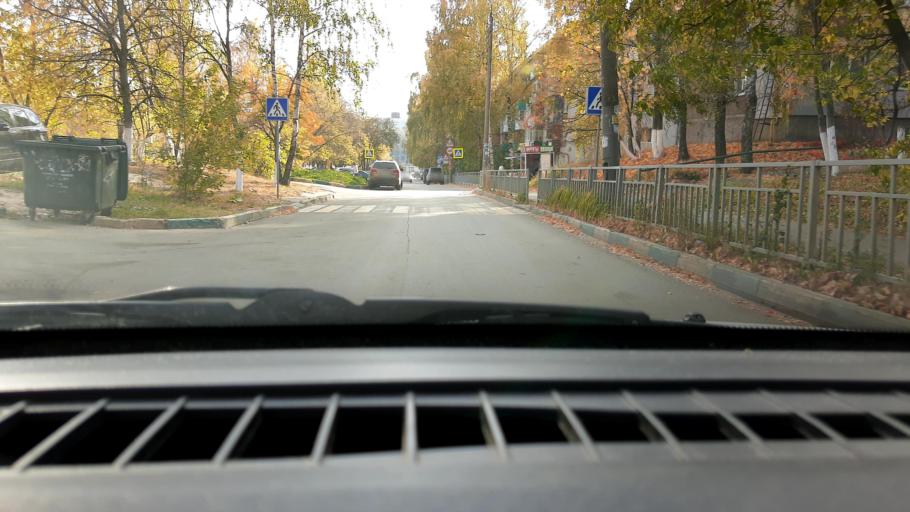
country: RU
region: Nizjnij Novgorod
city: Nizhniy Novgorod
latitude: 56.2344
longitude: 43.9558
